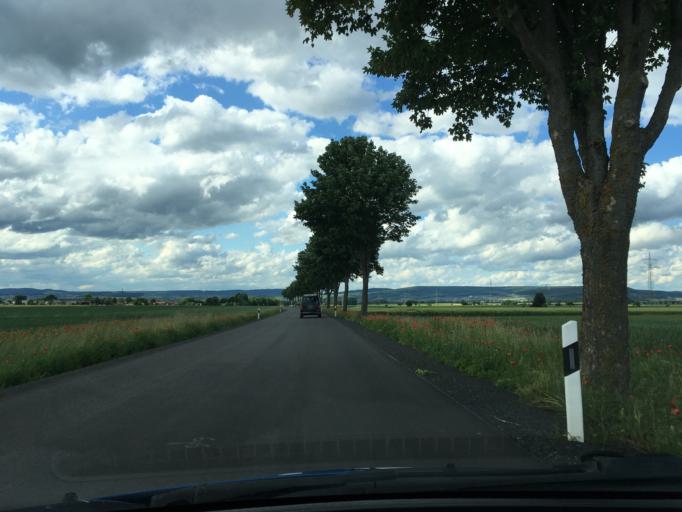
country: DE
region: Lower Saxony
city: Moringen
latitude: 51.7564
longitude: 9.8726
